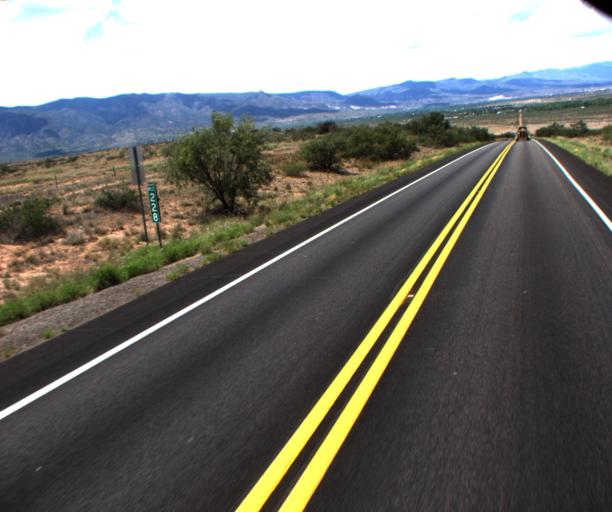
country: US
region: Arizona
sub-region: Yavapai County
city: Camp Verde
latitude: 34.5078
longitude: -111.7669
